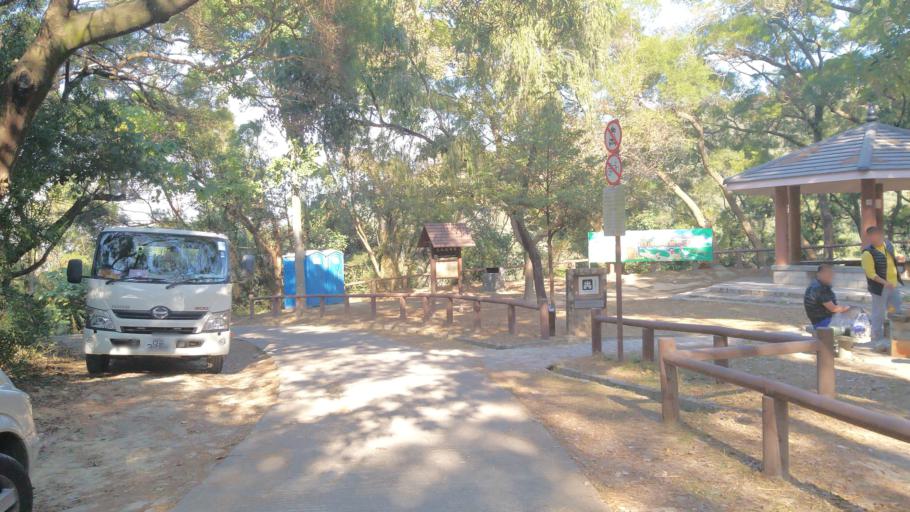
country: HK
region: Tuen Mun
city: Tuen Mun
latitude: 22.4068
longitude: 113.9883
